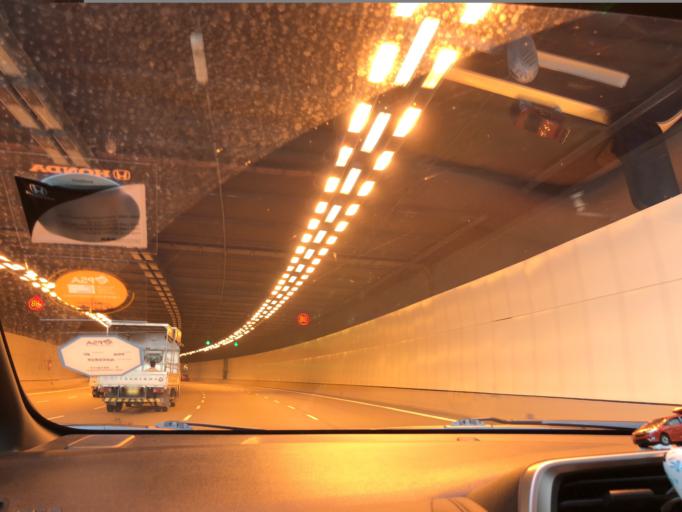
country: SG
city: Singapore
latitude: 1.2705
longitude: 103.8595
